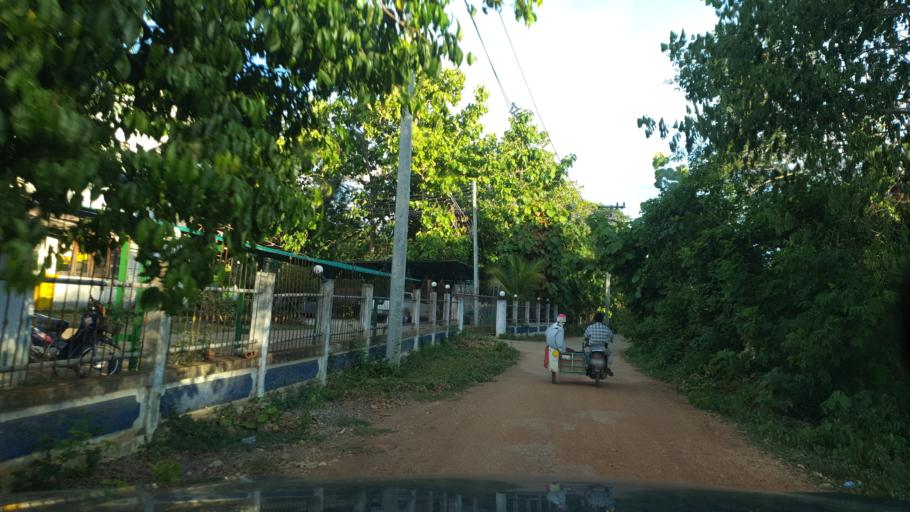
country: TH
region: Lampang
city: Sop Prap
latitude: 17.9519
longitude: 99.3497
